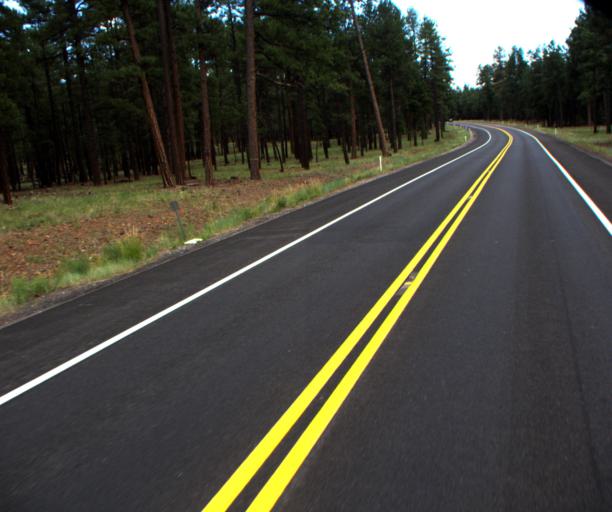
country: US
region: Arizona
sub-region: Coconino County
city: Flagstaff
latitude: 35.2528
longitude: -111.6989
